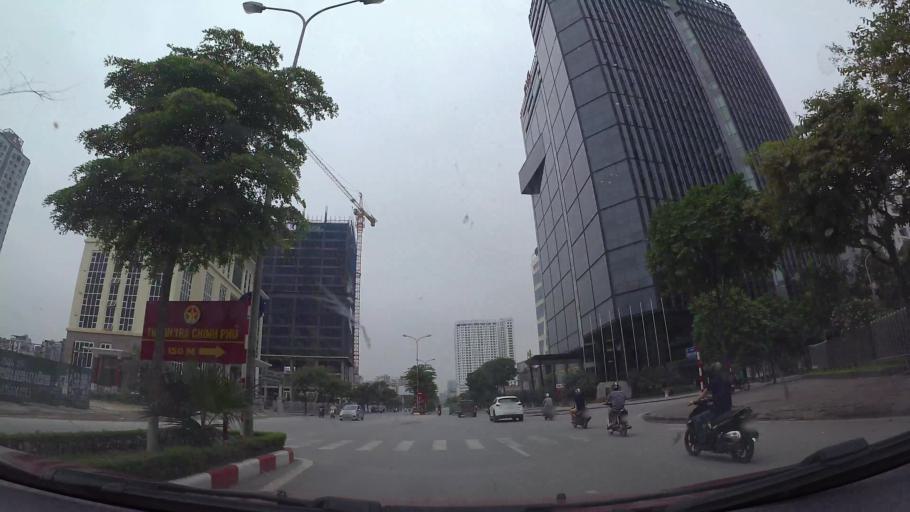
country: VN
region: Ha Noi
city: Cau Giay
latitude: 21.0248
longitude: 105.7889
